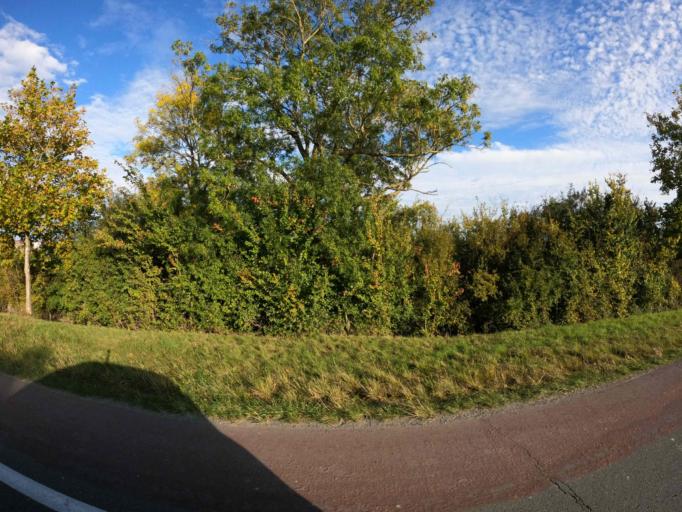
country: FR
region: Poitou-Charentes
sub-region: Departement de la Charente-Maritime
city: Marans
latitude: 46.2860
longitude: -0.9934
